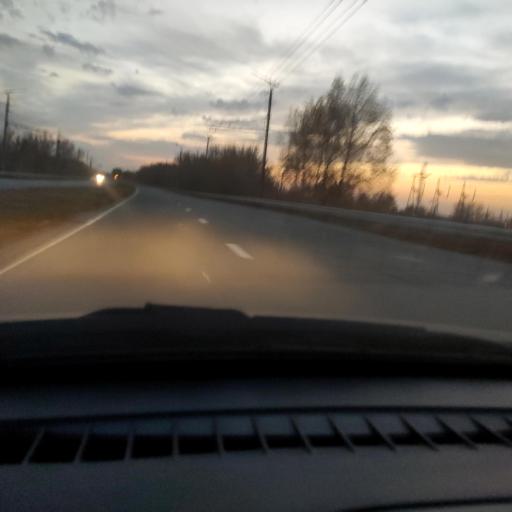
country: RU
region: Samara
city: Zhigulevsk
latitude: 53.5477
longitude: 49.5896
